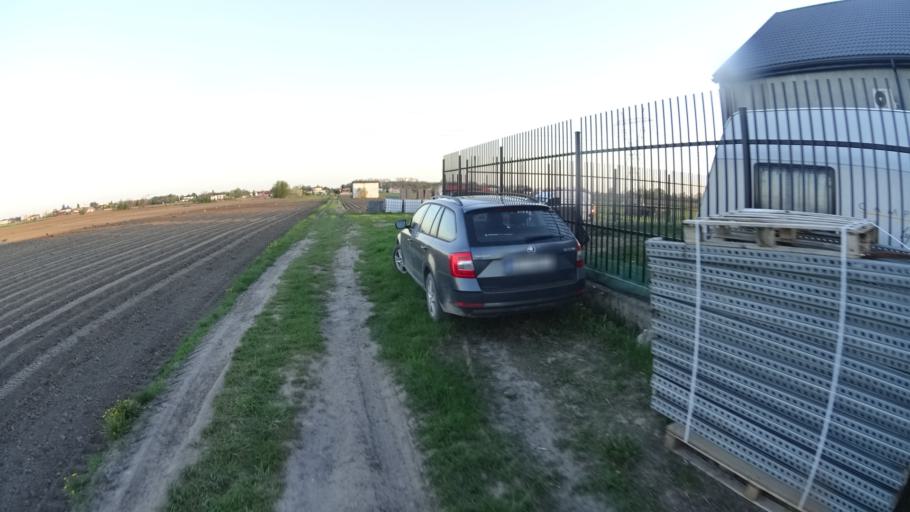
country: PL
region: Masovian Voivodeship
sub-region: Powiat warszawski zachodni
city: Ozarow Mazowiecki
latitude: 52.2281
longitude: 20.7819
